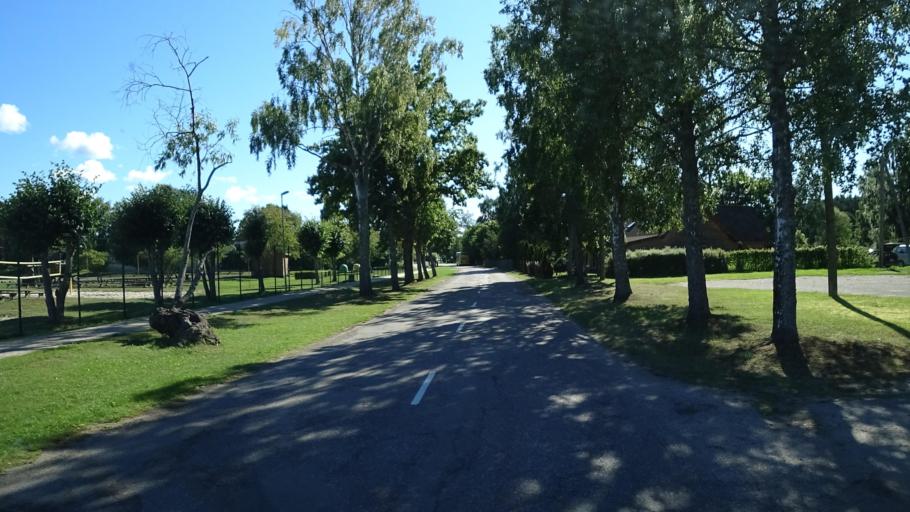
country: LV
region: Dundaga
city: Dundaga
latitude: 57.7452
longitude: 22.5885
